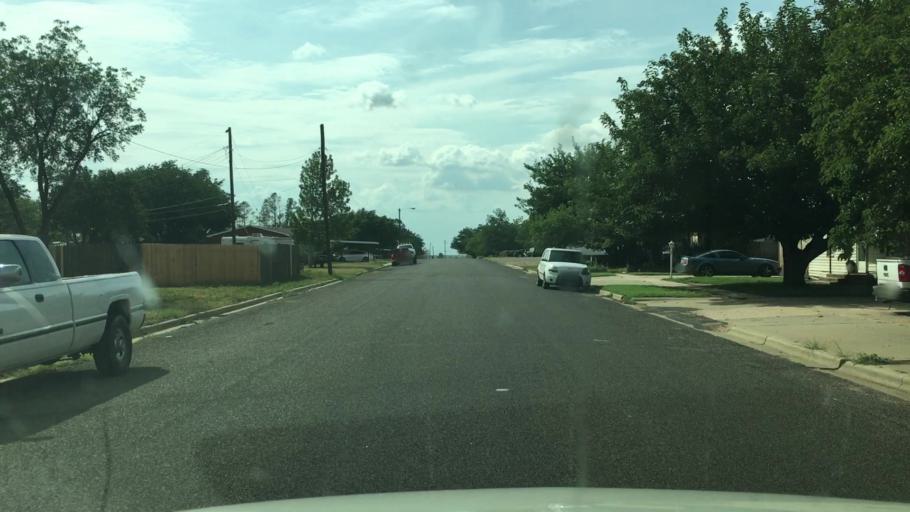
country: US
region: Texas
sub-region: Dawson County
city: Lamesa
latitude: 32.7521
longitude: -101.9534
